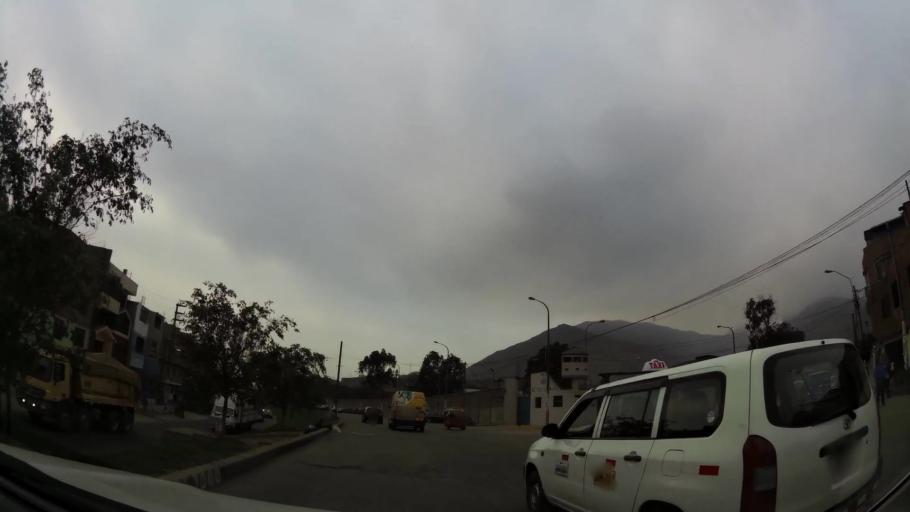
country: PE
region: Lima
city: Lima
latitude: -12.0095
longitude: -76.9968
